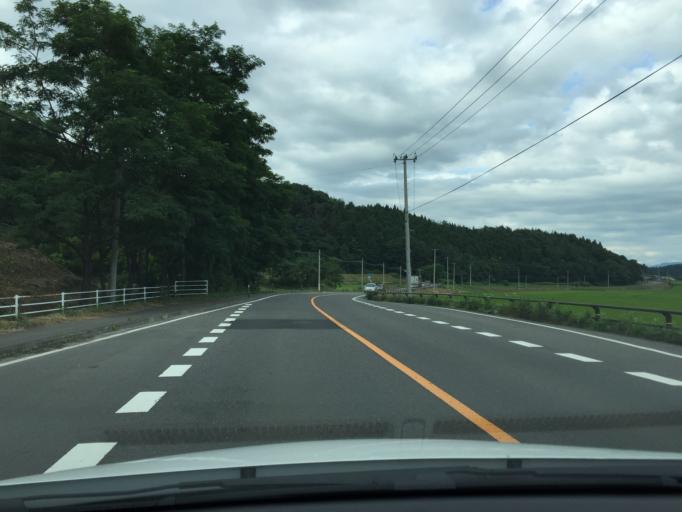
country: JP
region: Fukushima
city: Sukagawa
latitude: 37.1961
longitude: 140.2289
